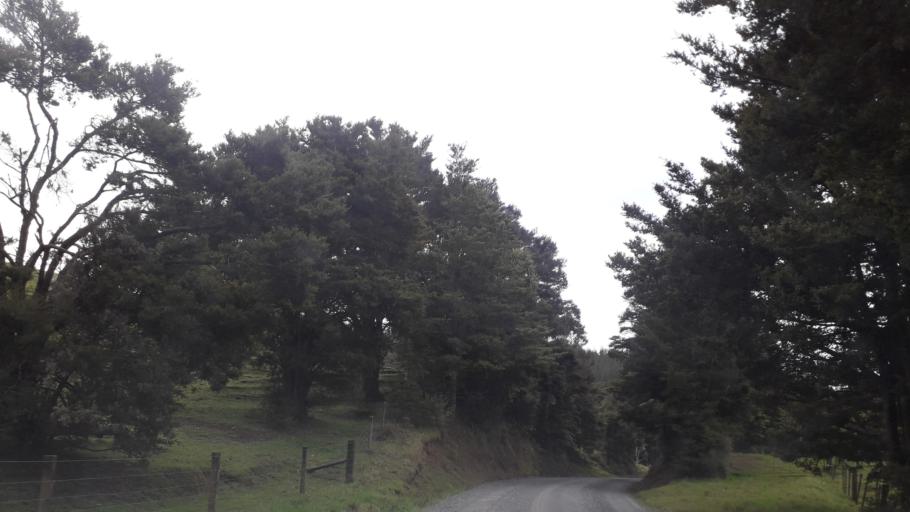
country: NZ
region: Northland
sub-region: Far North District
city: Taipa
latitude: -35.0506
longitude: 173.5584
